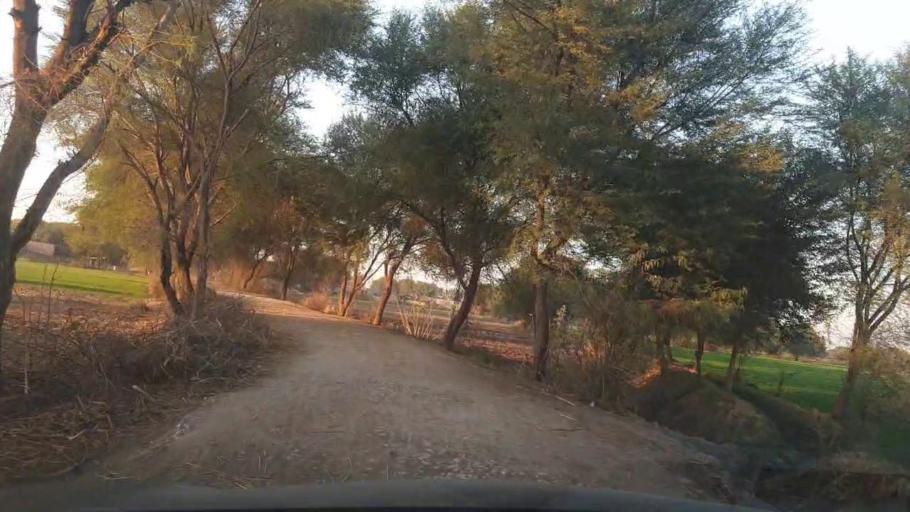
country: PK
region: Sindh
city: Ubauro
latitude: 28.1855
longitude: 69.6023
